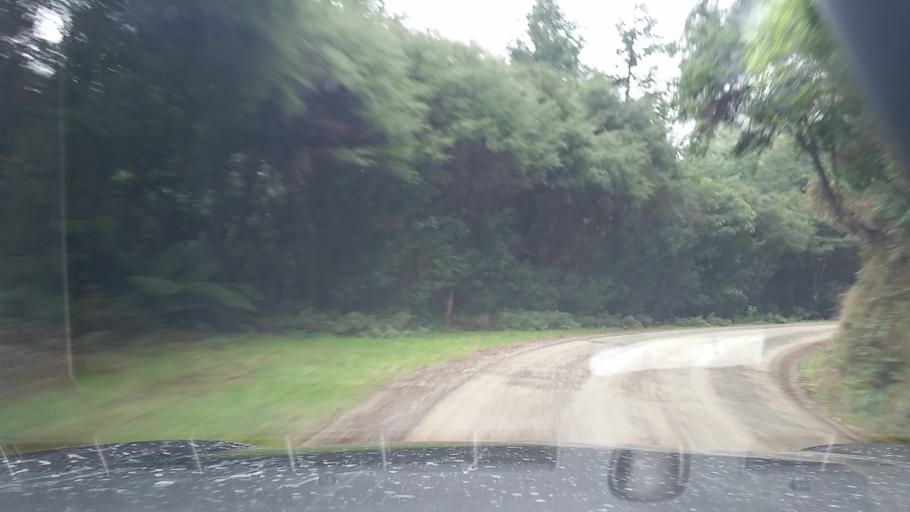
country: NZ
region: Marlborough
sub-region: Marlborough District
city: Picton
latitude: -41.1801
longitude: 173.9991
